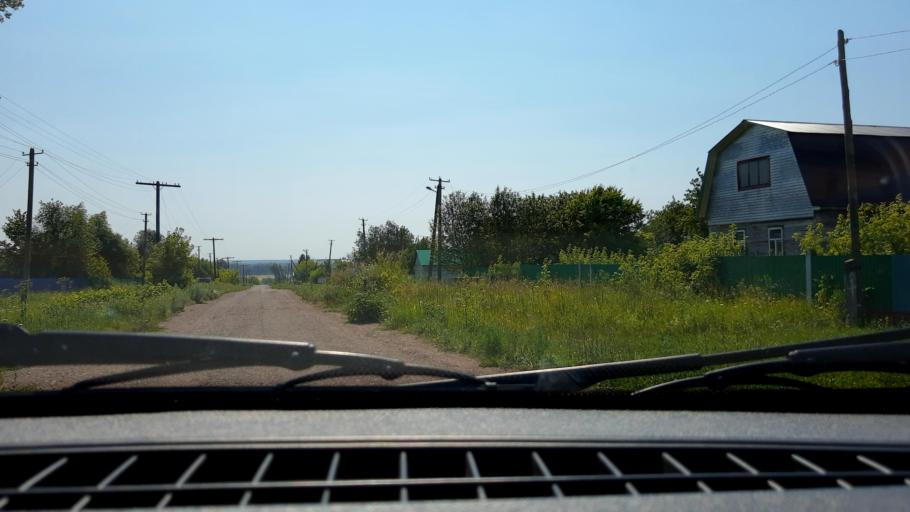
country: RU
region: Bashkortostan
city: Kushnarenkovo
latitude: 55.0753
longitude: 55.1701
